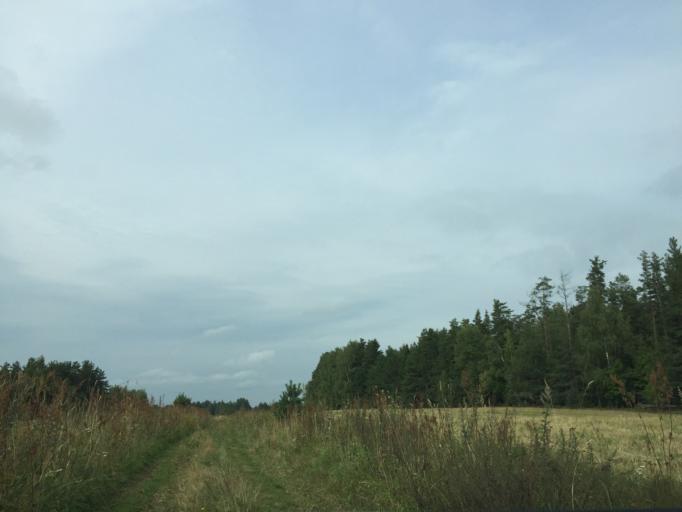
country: LV
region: Cibla
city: Cibla
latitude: 56.2419
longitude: 27.8273
